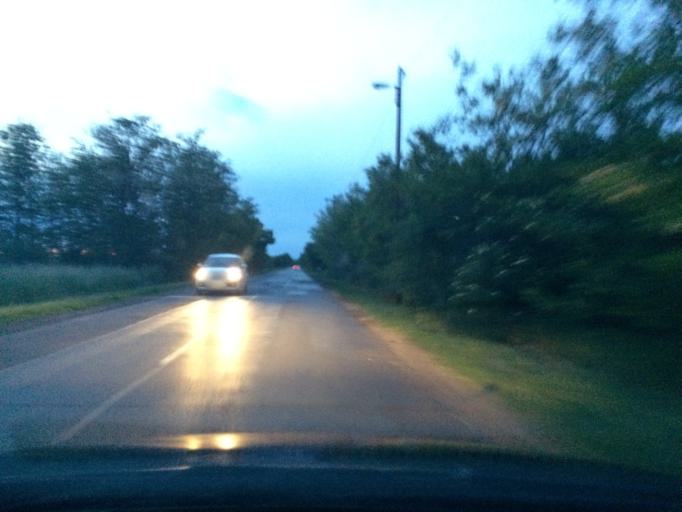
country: HU
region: Hajdu-Bihar
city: Hajdunanas
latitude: 47.9109
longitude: 21.4005
